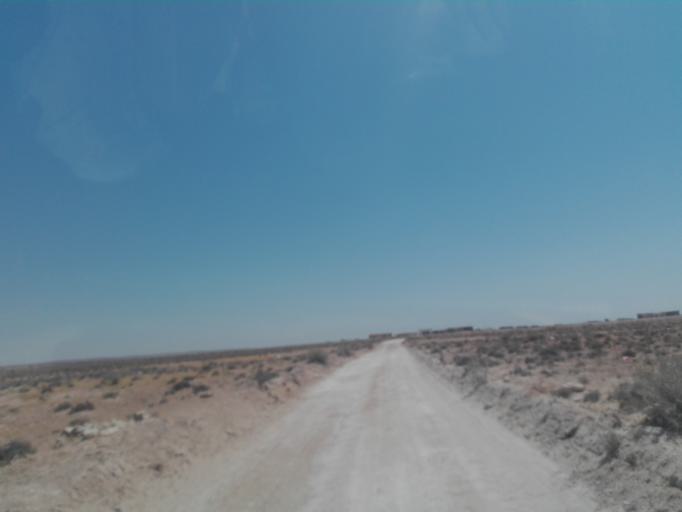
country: TN
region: Safaqis
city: Skhira
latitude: 34.4190
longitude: 9.9573
